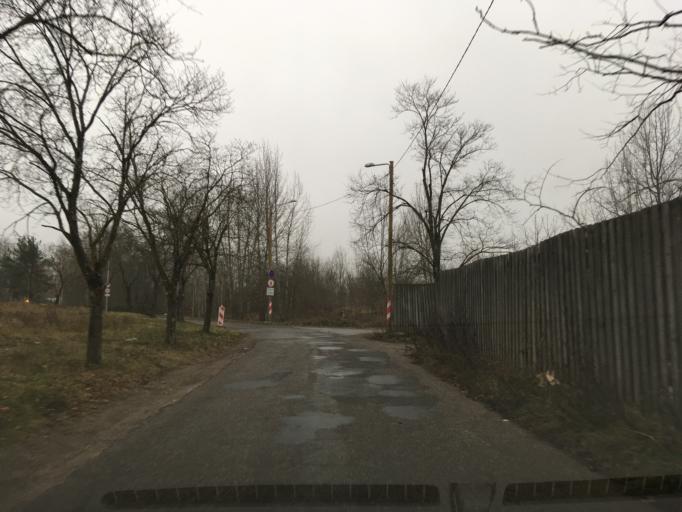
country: EE
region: Harju
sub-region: Tallinna linn
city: Tallinn
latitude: 59.3984
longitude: 24.7184
